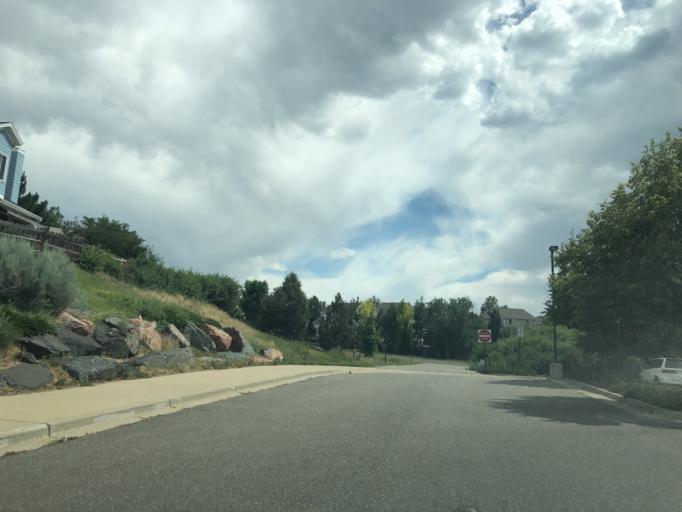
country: US
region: Colorado
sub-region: Arapahoe County
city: Dove Valley
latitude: 39.6173
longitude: -104.7674
